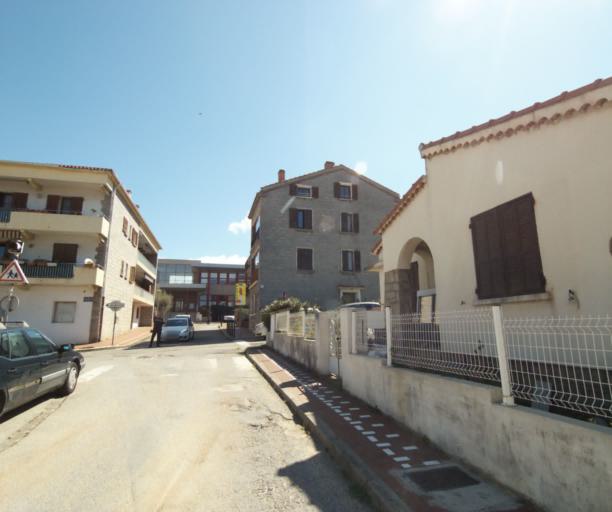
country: FR
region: Corsica
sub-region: Departement de la Corse-du-Sud
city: Propriano
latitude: 41.6755
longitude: 8.9064
